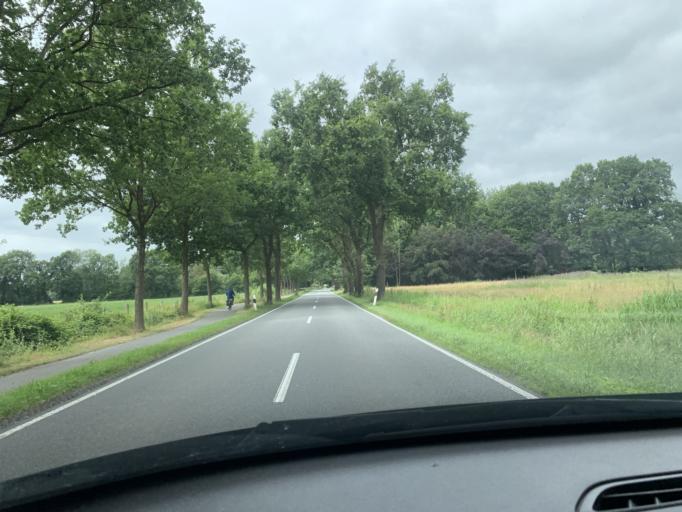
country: DE
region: Lower Saxony
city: Wiefelstede
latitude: 53.2017
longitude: 8.1216
